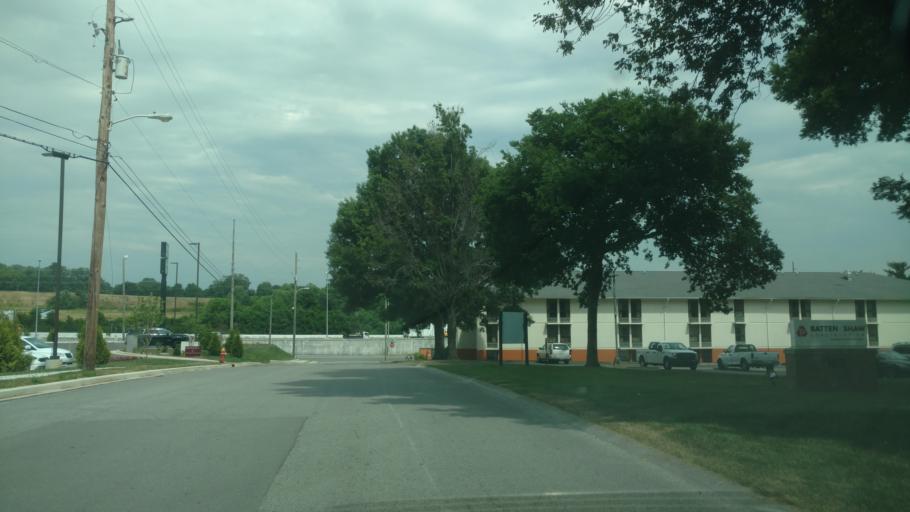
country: US
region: Tennessee
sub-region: Davidson County
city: Lakewood
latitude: 36.2228
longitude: -86.6957
